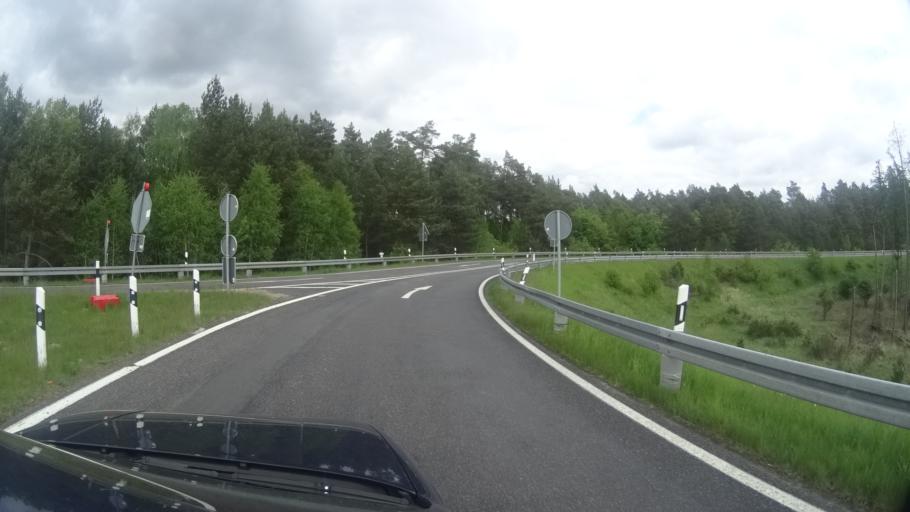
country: DE
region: Mecklenburg-Vorpommern
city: Malchow
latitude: 53.4591
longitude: 12.3848
